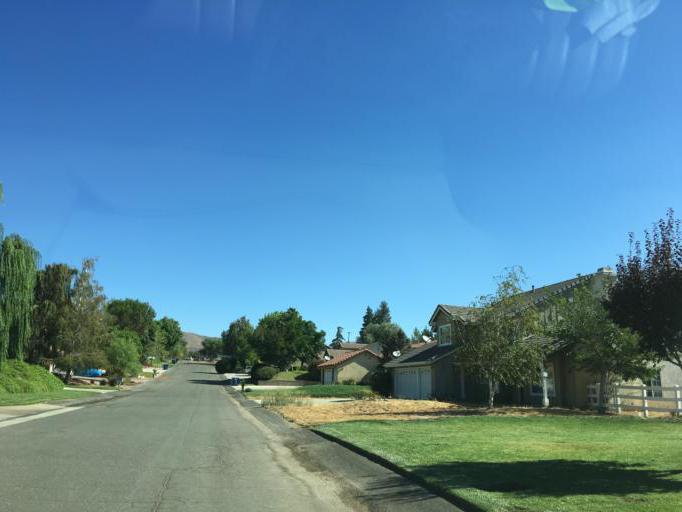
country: US
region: California
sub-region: Los Angeles County
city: Acton
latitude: 34.4789
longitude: -118.1990
